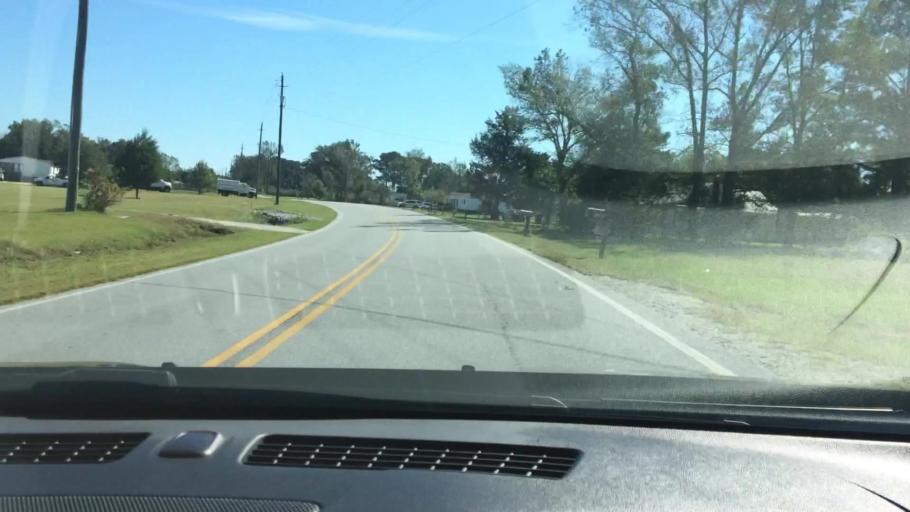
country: US
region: North Carolina
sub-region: Pitt County
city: Grifton
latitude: 35.3779
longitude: -77.3674
